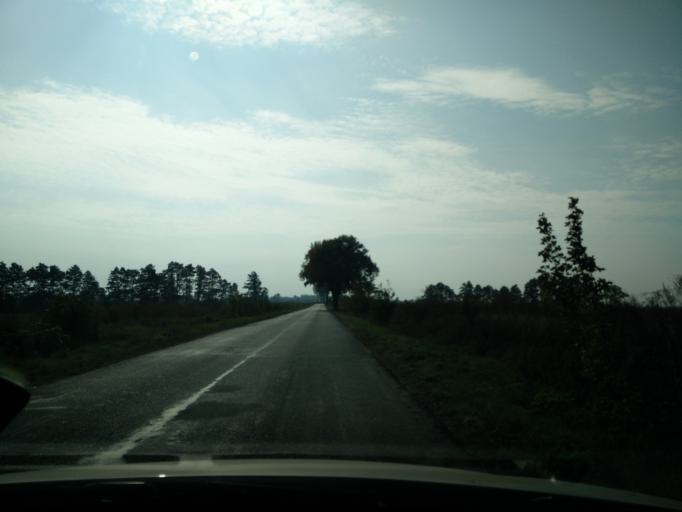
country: PL
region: Greater Poland Voivodeship
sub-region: Powiat sredzki
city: Dominowo
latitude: 52.2792
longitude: 17.3206
